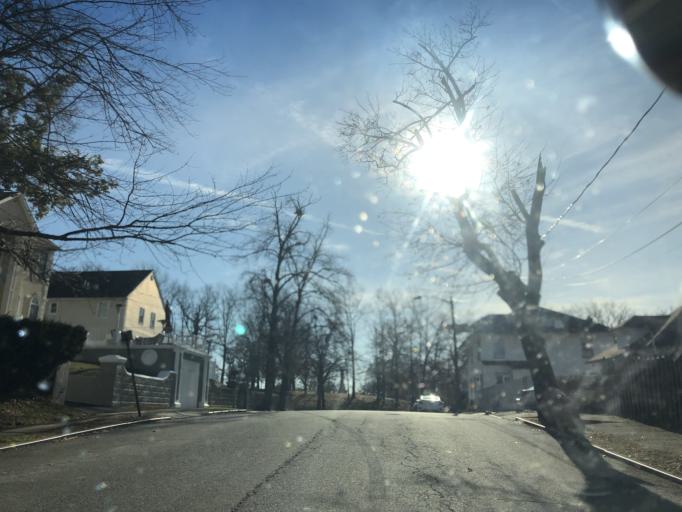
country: US
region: New Jersey
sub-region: Bergen County
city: Fair Lawn
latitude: 40.9190
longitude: -74.1379
